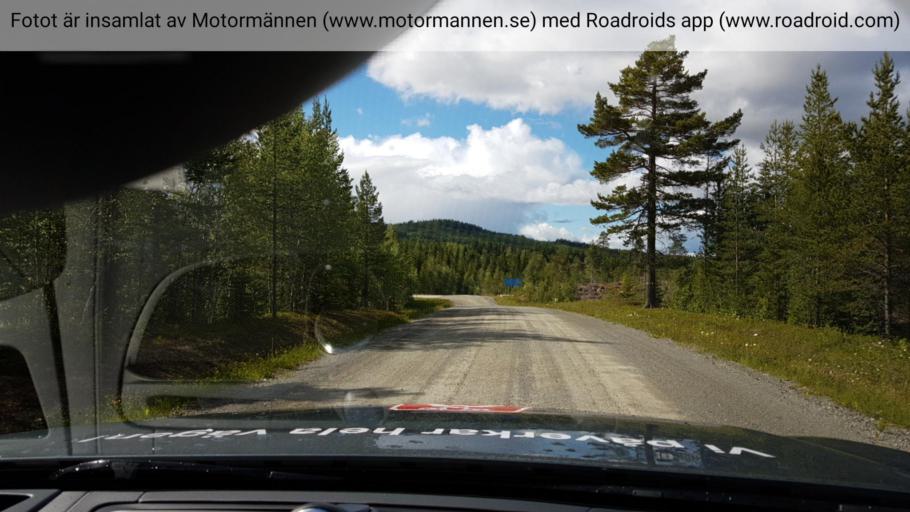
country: SE
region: Jaemtland
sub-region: Bergs Kommun
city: Hoverberg
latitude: 63.0276
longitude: 14.0748
